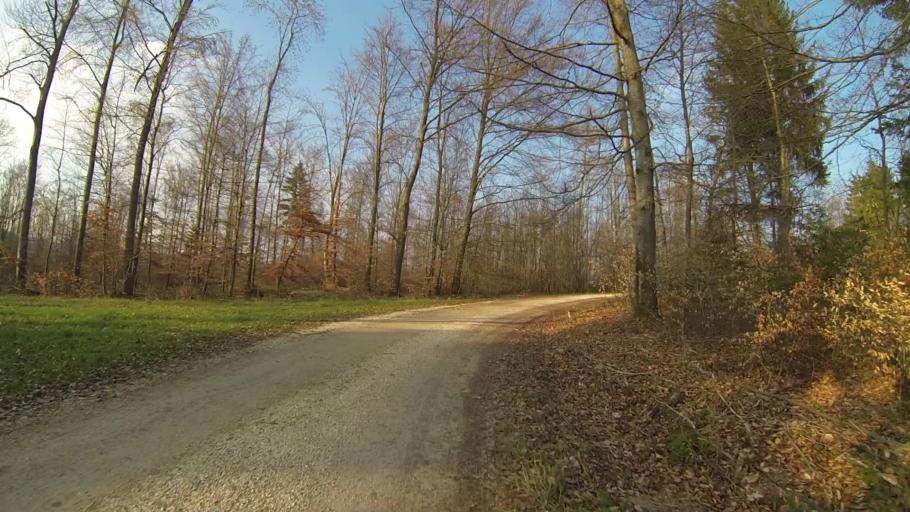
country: DE
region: Baden-Wuerttemberg
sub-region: Regierungsbezirk Stuttgart
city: Heidenheim an der Brenz
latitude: 48.6887
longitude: 10.1682
